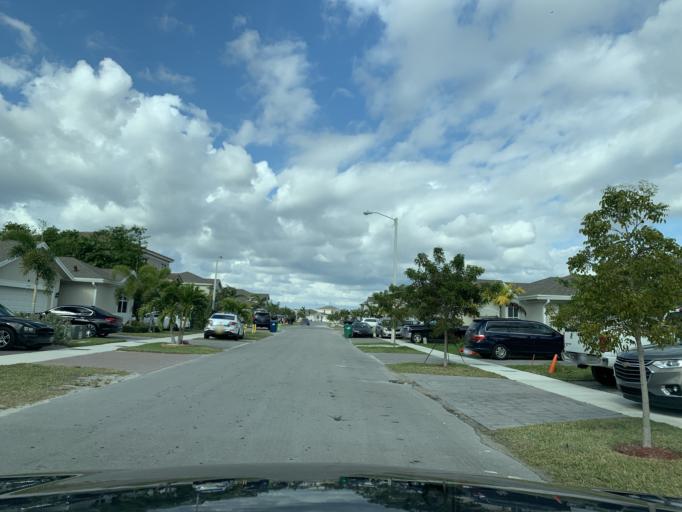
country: US
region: Florida
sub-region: Miami-Dade County
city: Naranja
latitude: 25.5101
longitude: -80.4090
